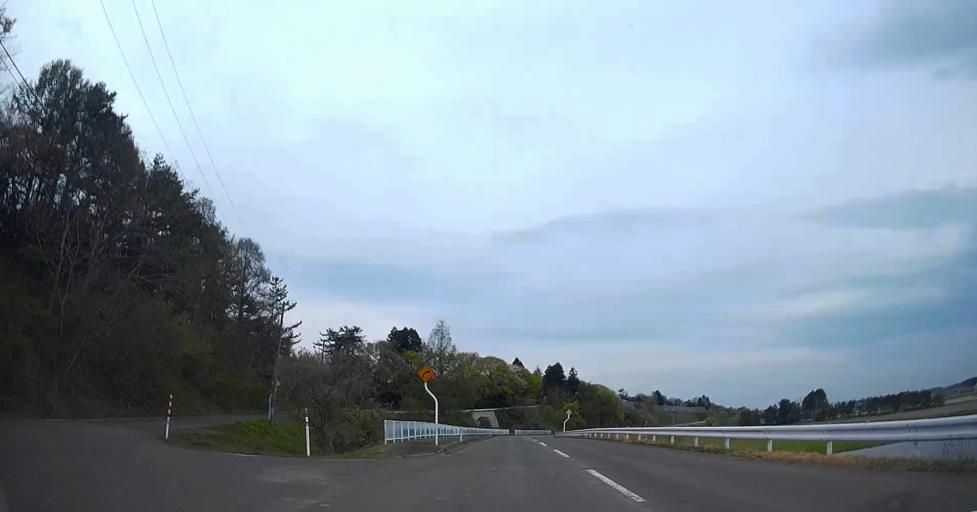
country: JP
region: Aomori
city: Goshogawara
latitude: 40.8994
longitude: 140.4909
